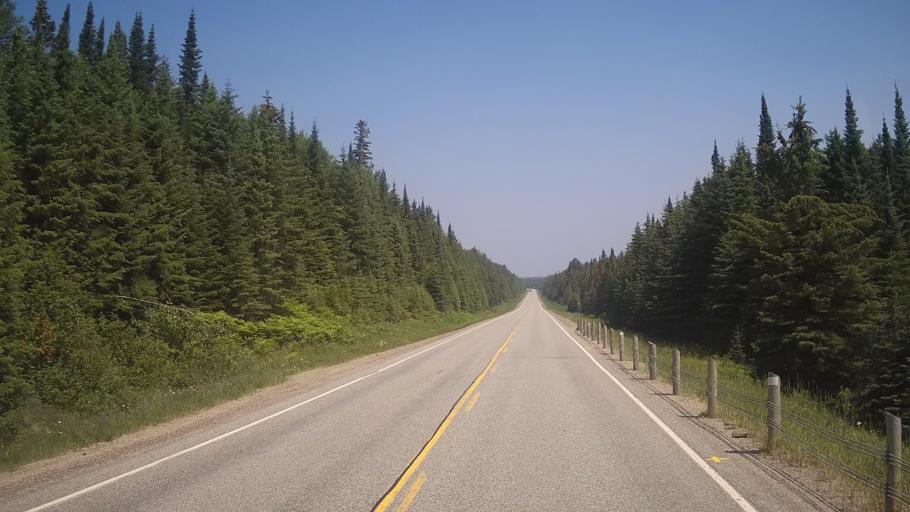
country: CA
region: Ontario
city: Timmins
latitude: 48.2040
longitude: -81.5778
